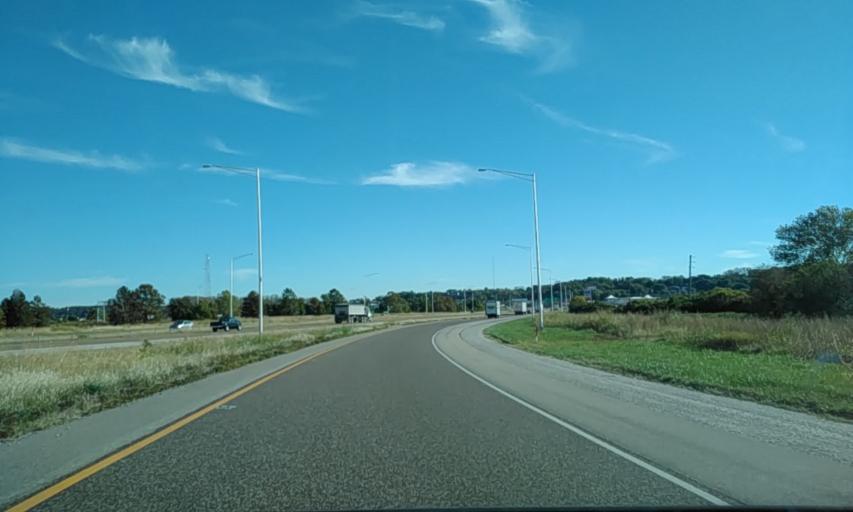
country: US
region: Illinois
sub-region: Saint Clair County
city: Caseyville
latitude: 38.6730
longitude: -90.0273
